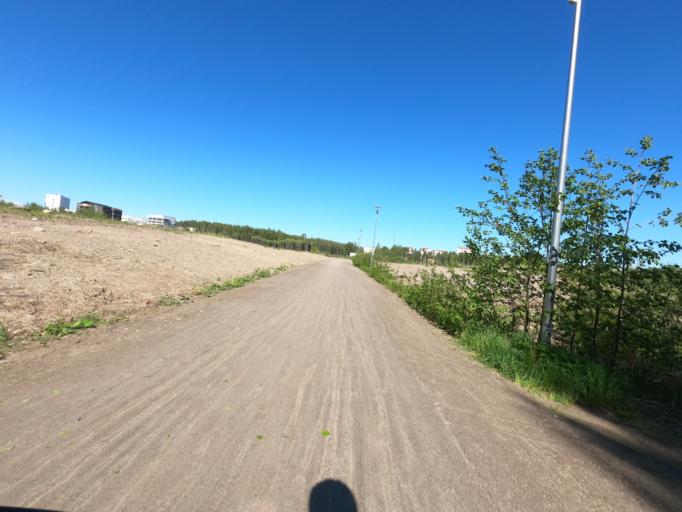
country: FI
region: North Karelia
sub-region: Joensuu
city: Joensuu
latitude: 62.5869
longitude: 29.7594
